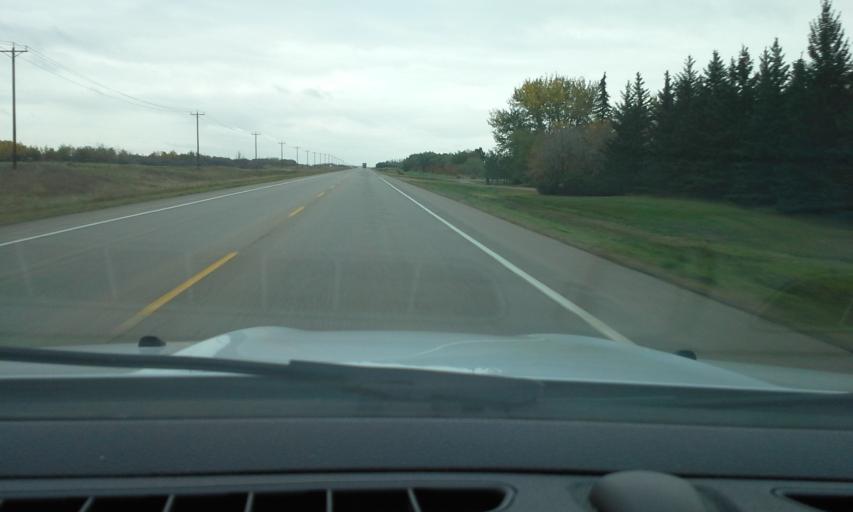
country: CA
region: Saskatchewan
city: Lloydminster
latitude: 53.2780
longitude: -109.8449
